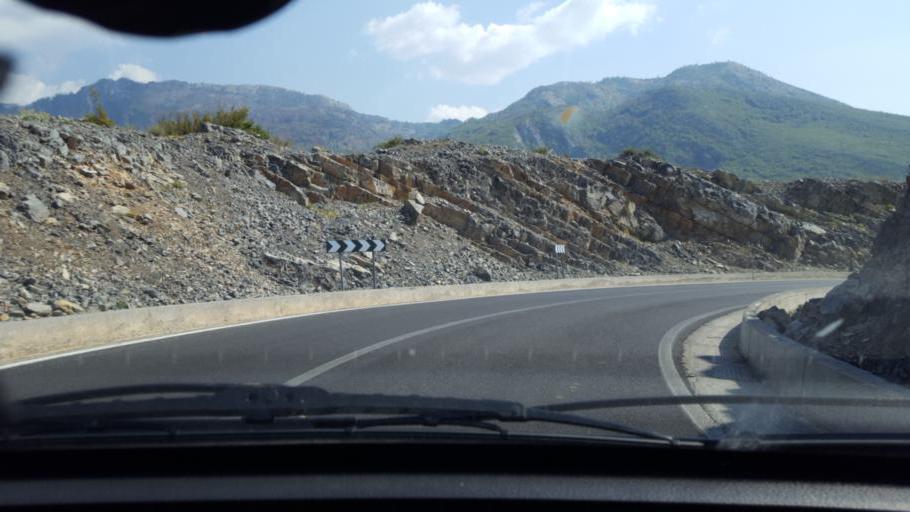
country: AL
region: Shkoder
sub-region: Rrethi i Malesia e Madhe
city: Kastrat
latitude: 42.4111
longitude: 19.5044
